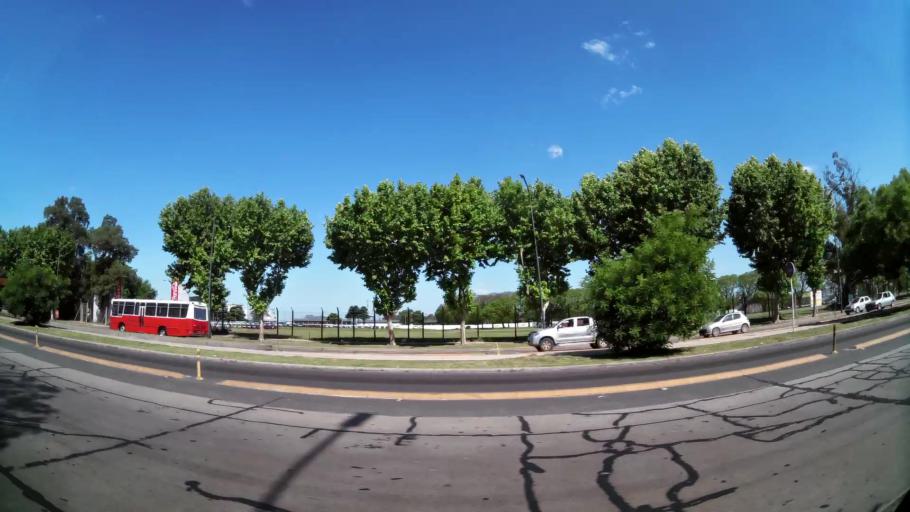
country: AR
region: Buenos Aires F.D.
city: Villa Lugano
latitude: -34.6951
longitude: -58.4671
